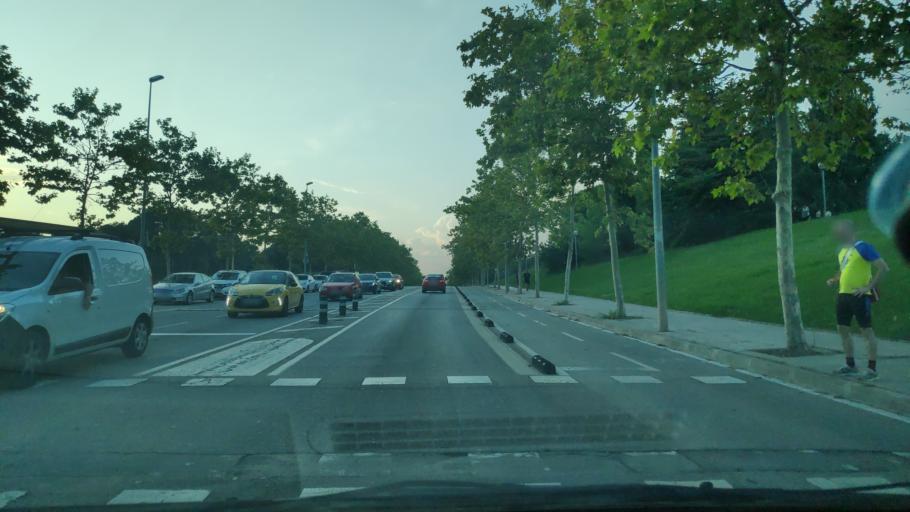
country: ES
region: Catalonia
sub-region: Provincia de Barcelona
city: Cerdanyola del Valles
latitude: 41.4840
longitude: 2.1398
